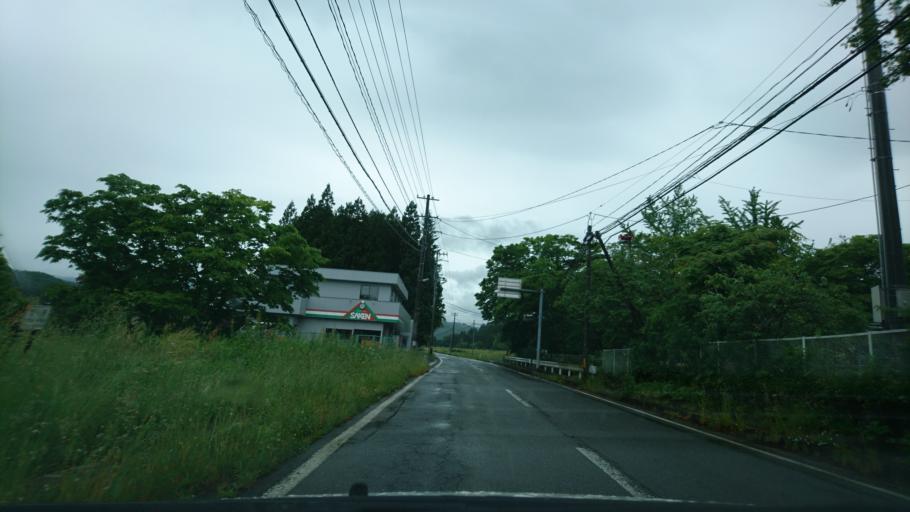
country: JP
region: Iwate
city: Ichinoseki
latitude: 38.9745
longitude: 140.9396
